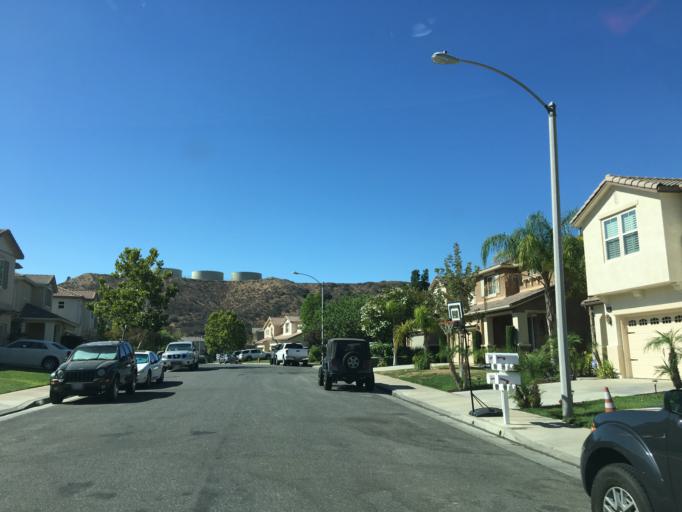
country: US
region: California
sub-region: Los Angeles County
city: Santa Clarita
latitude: 34.4442
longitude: -118.4805
